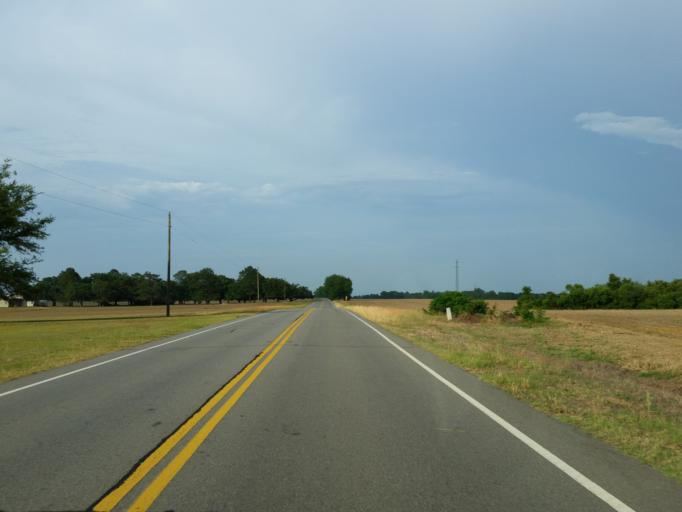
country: US
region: Georgia
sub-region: Dooly County
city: Vienna
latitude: 32.1622
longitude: -83.7840
